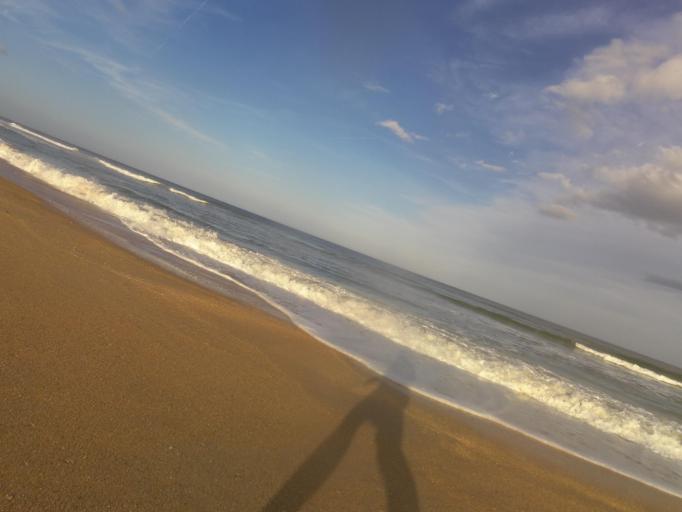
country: US
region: Florida
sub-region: Flagler County
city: Palm Coast
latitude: 29.6294
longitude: -81.1961
